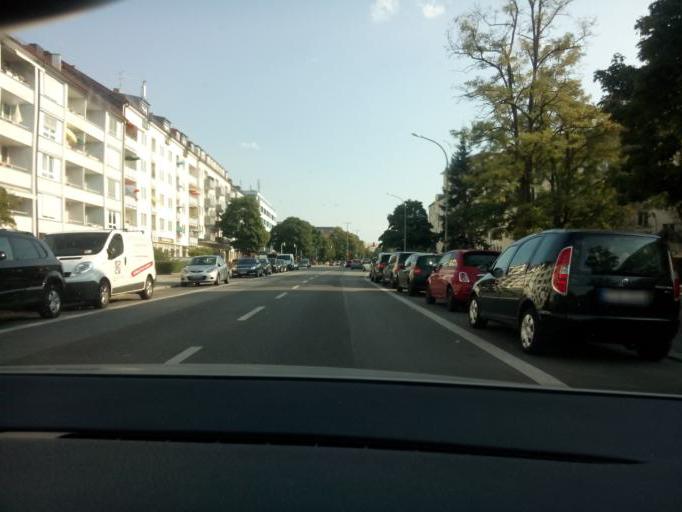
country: DE
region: Bavaria
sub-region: Upper Bavaria
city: Munich
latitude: 48.1102
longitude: 11.6040
